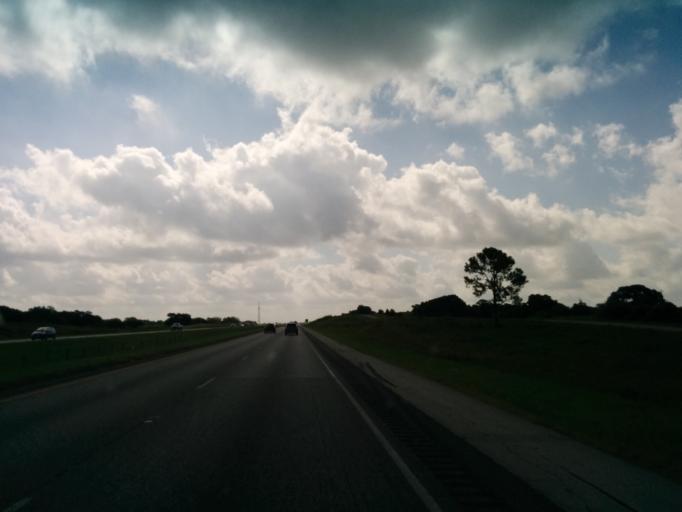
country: US
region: Texas
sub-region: Fayette County
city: Flatonia
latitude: 29.6950
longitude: -97.0284
